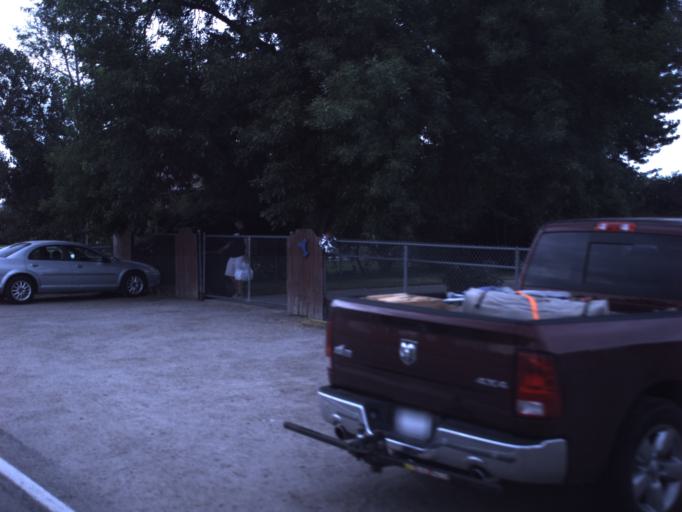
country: US
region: Utah
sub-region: Davis County
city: West Point
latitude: 41.1296
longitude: -112.1126
